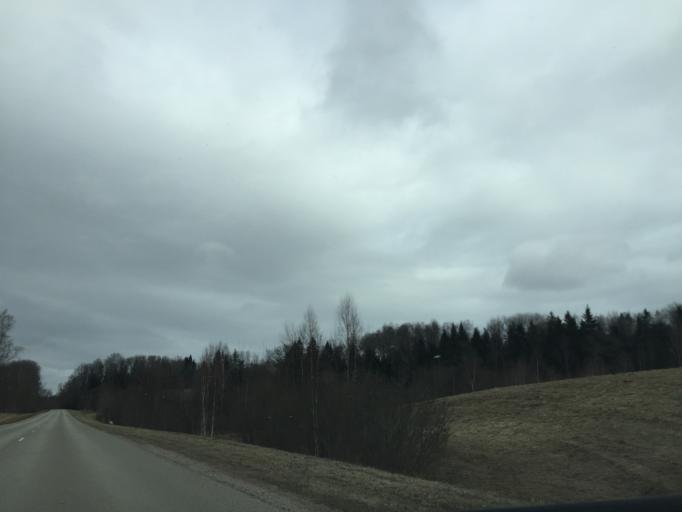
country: LV
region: Kraslavas Rajons
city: Kraslava
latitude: 55.9461
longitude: 27.1627
